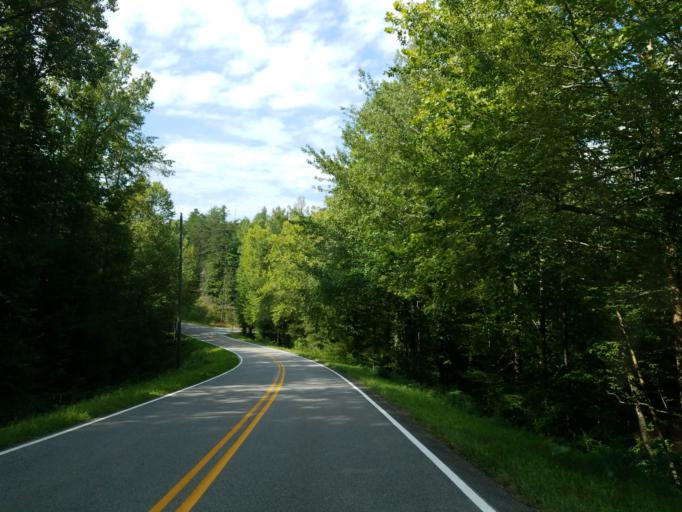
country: US
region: Georgia
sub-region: Gilmer County
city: Ellijay
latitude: 34.7482
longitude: -84.4203
